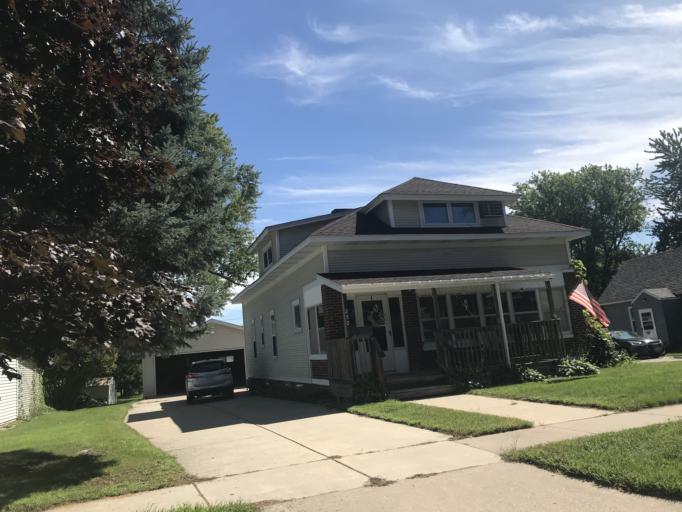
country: US
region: Wisconsin
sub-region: Marinette County
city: Peshtigo
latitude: 45.0519
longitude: -87.7510
